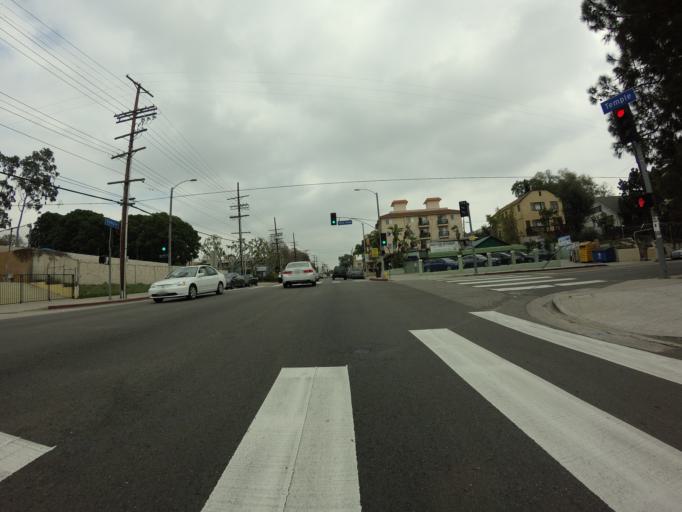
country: US
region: California
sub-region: Los Angeles County
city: Echo Park
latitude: 34.0716
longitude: -118.2721
